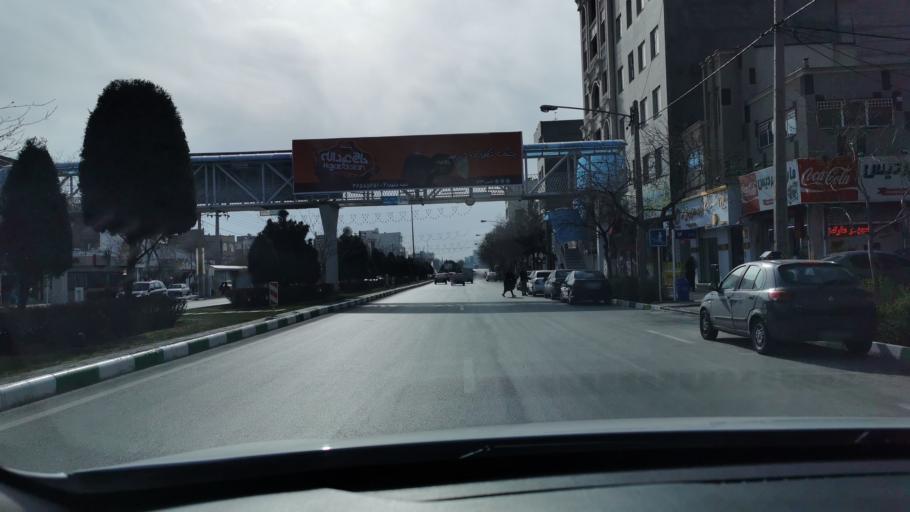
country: IR
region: Razavi Khorasan
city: Mashhad
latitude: 36.2970
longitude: 59.5274
